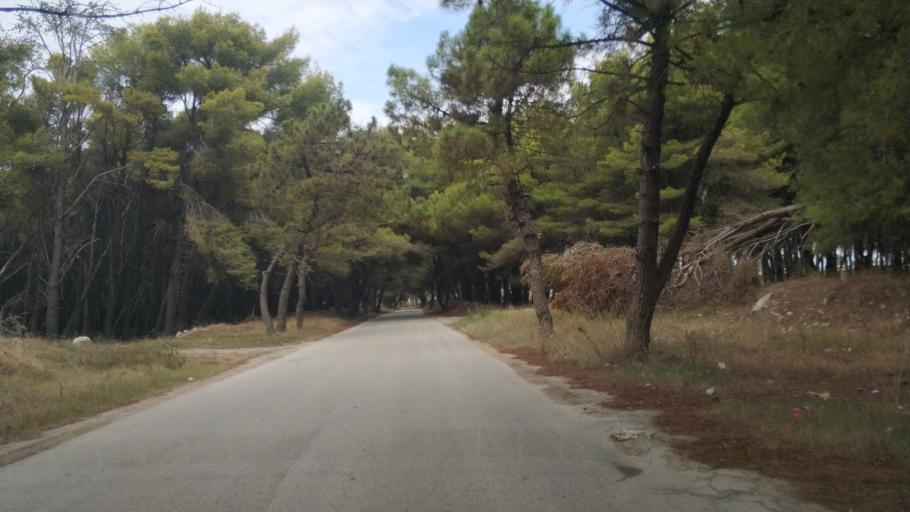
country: AL
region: Vlore
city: Vlore
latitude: 40.4678
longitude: 19.4609
